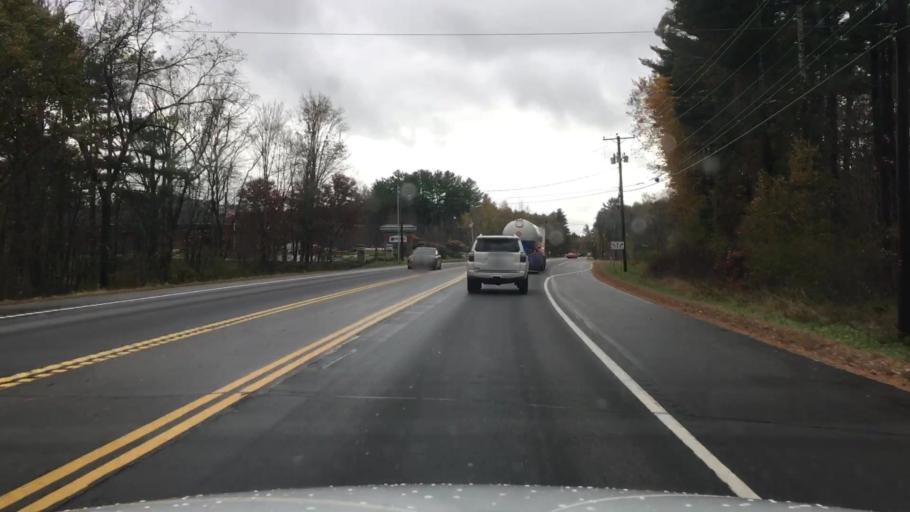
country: US
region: New Hampshire
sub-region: Strafford County
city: Lee
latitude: 43.1432
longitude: -71.0093
